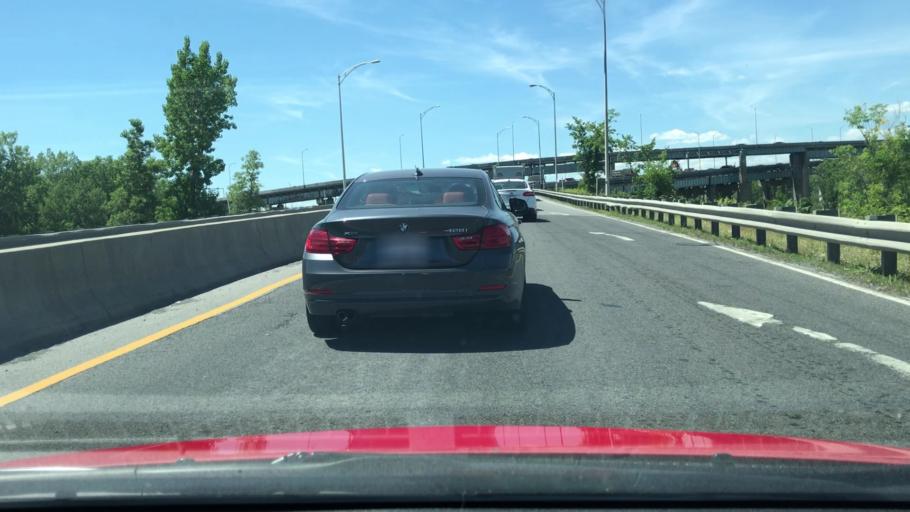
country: CA
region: Quebec
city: Montreal-Ouest
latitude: 45.4053
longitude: -73.6561
